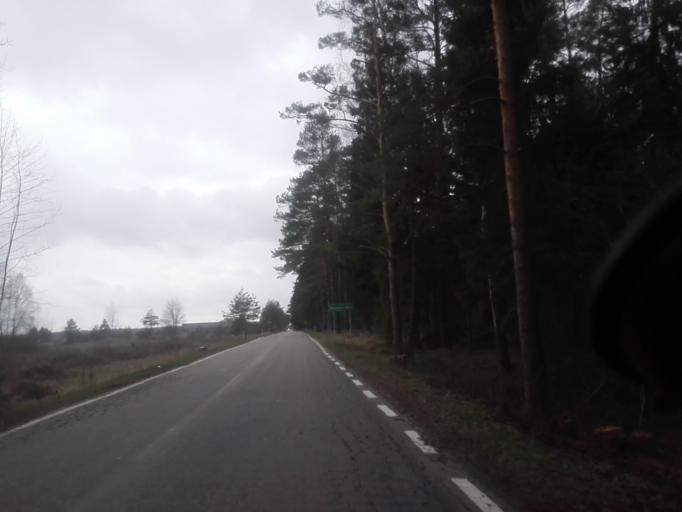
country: PL
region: Podlasie
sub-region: Powiat sejnenski
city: Krasnopol
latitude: 54.1654
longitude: 23.2244
